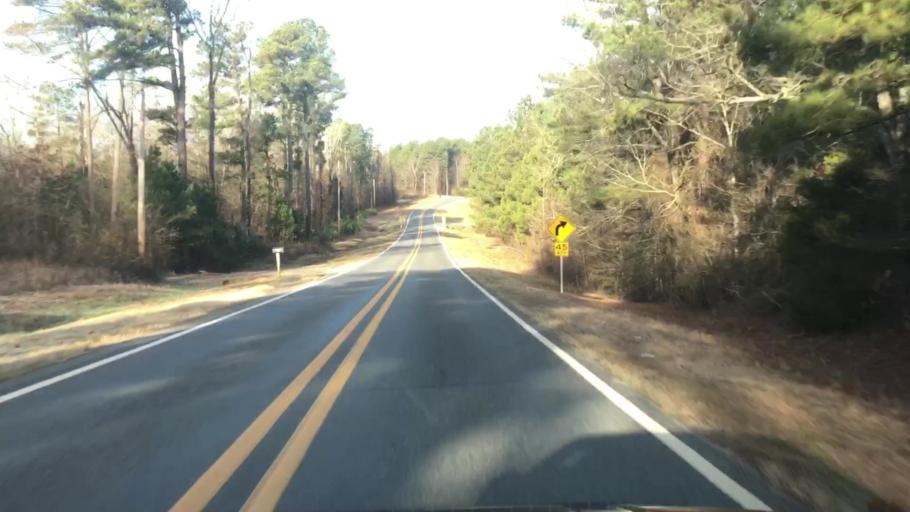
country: US
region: Arkansas
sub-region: Garland County
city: Rockwell
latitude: 34.4779
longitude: -93.2676
